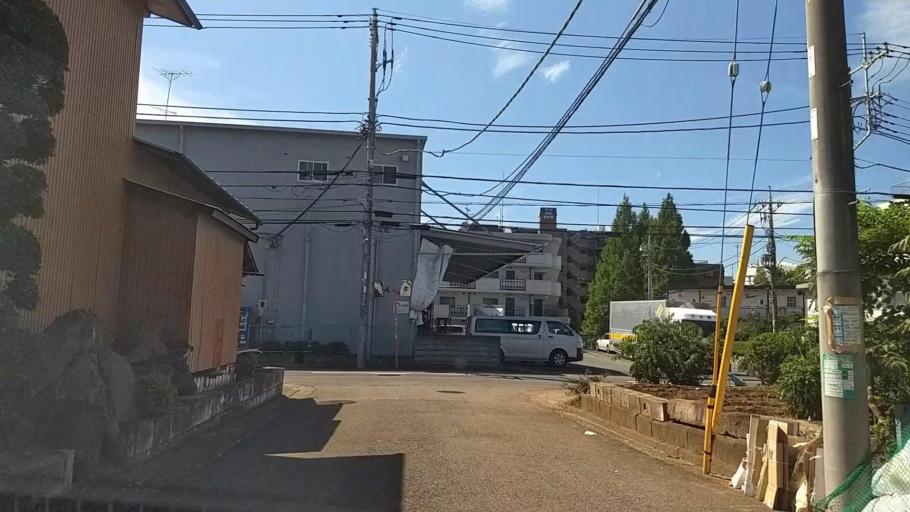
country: JP
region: Tokyo
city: Chofugaoka
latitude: 35.5610
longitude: 139.5629
